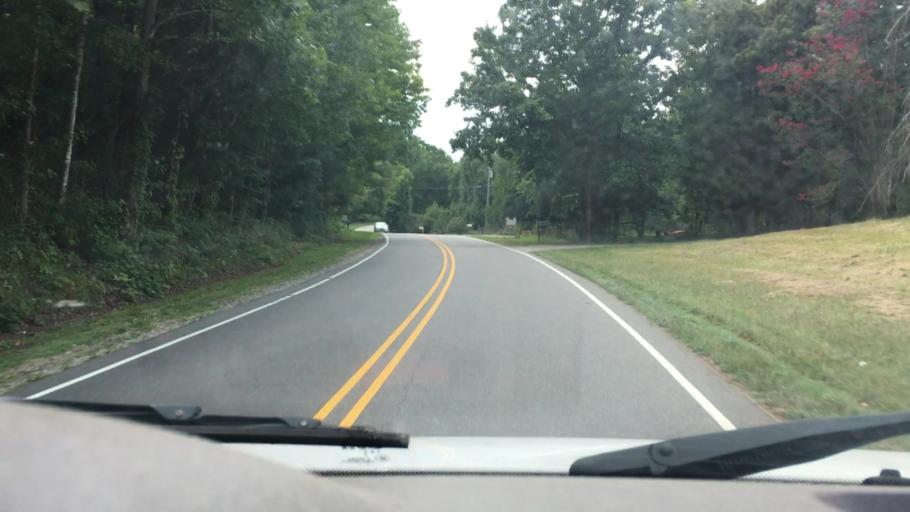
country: US
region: North Carolina
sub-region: Gaston County
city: Davidson
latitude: 35.4741
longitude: -80.7968
